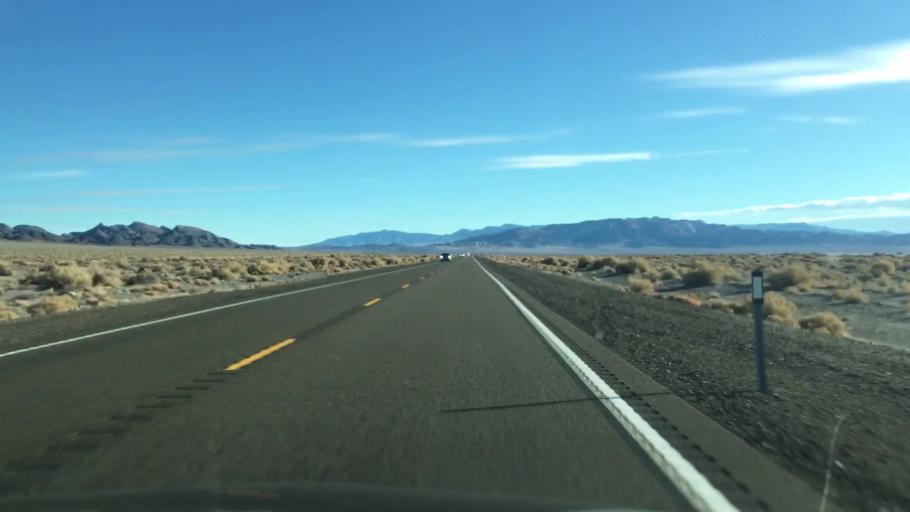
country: US
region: Nevada
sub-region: Nye County
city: Tonopah
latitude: 38.1121
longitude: -117.9292
